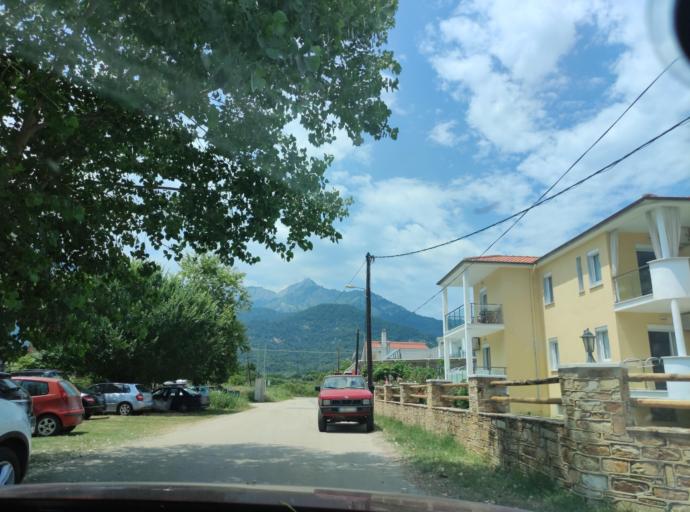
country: GR
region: East Macedonia and Thrace
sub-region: Nomos Kavalas
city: Potamia
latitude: 40.7242
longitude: 24.7563
